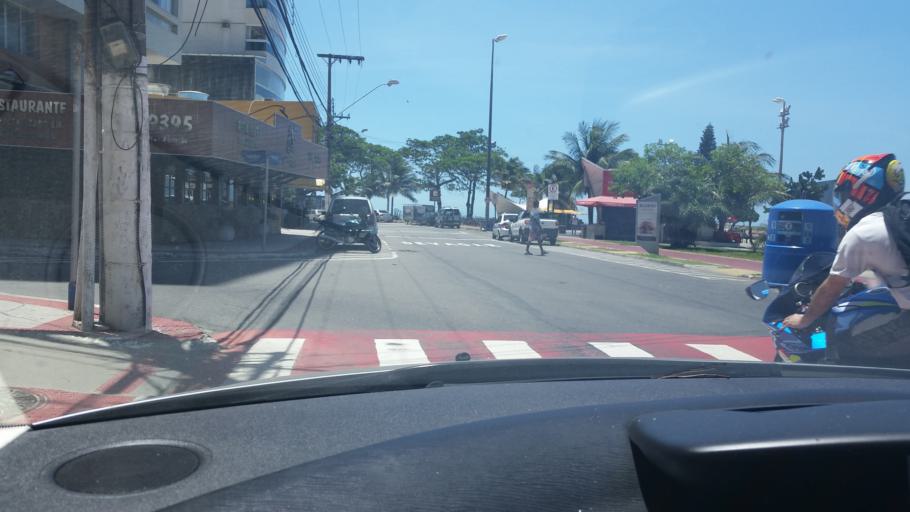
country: BR
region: Espirito Santo
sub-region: Vila Velha
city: Vila Velha
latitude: -20.3316
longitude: -40.2752
